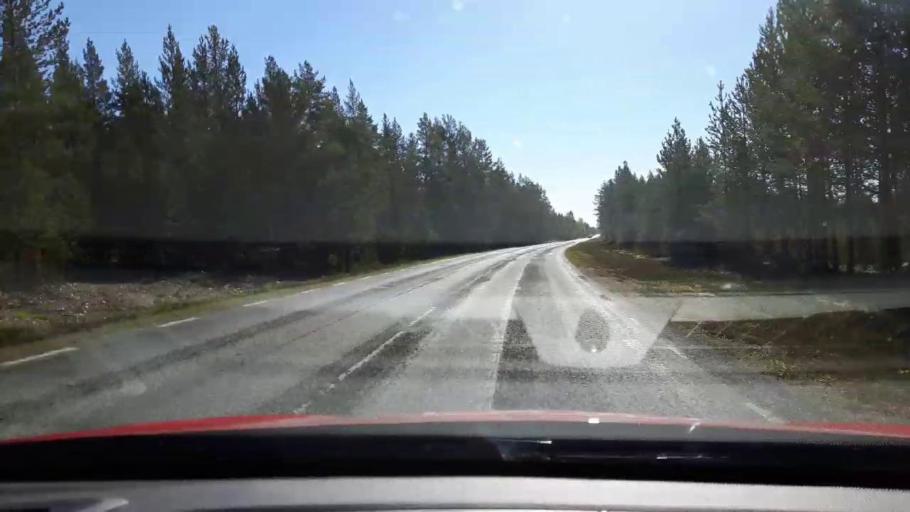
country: SE
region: Jaemtland
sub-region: Harjedalens Kommun
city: Sveg
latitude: 62.4222
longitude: 13.9057
